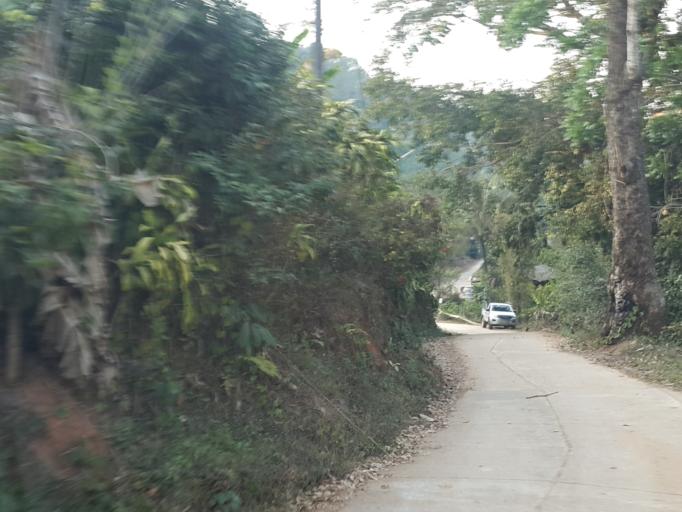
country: TH
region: Chiang Mai
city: Mae Taeng
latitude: 19.0648
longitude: 98.7756
